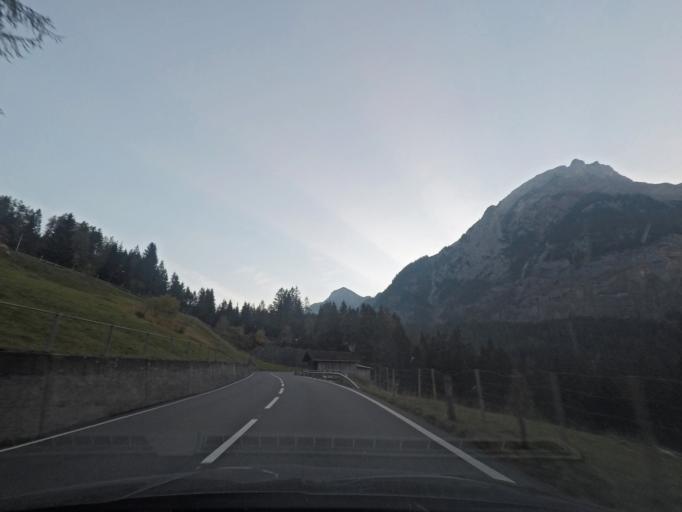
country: CH
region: Bern
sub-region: Frutigen-Niedersimmental District
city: Kandersteg
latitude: 46.5120
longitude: 7.6768
